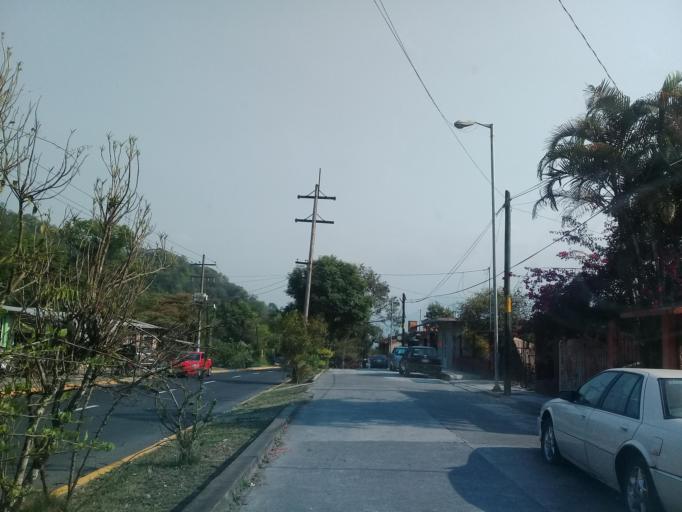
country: MX
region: Veracruz
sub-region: Ixtaczoquitlan
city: Campo Chico
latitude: 18.8522
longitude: -97.0390
